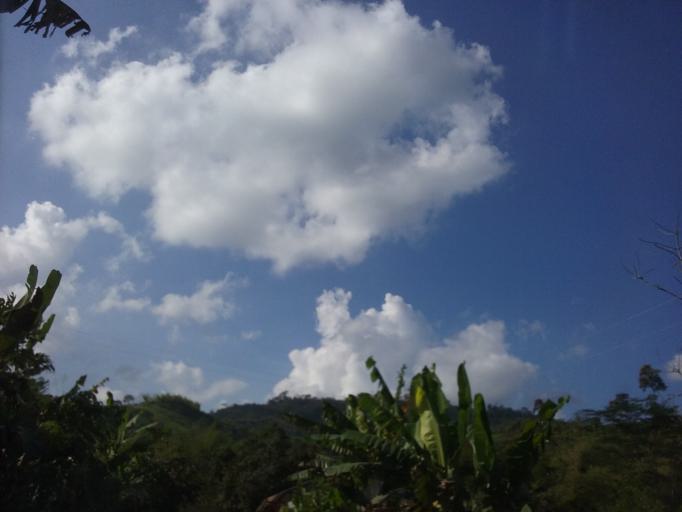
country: CO
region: Tolima
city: Libano
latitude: 4.8806
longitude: -75.0140
